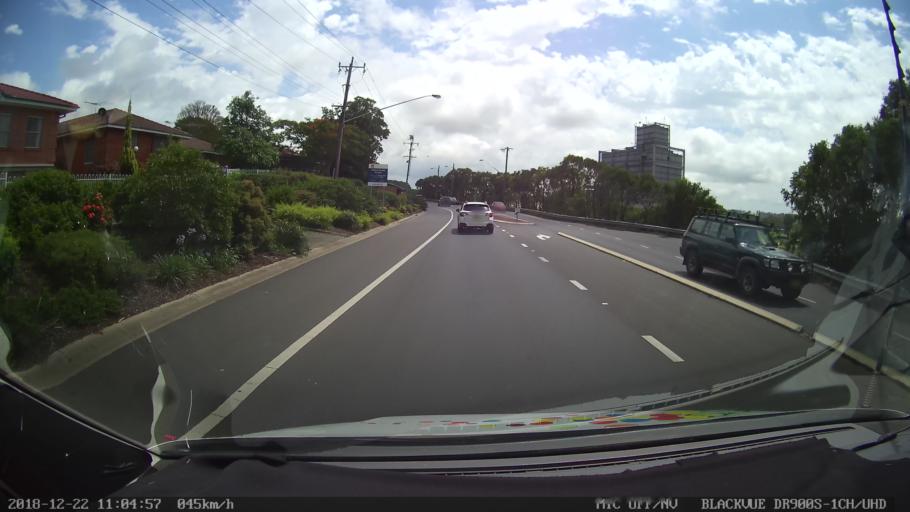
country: AU
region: New South Wales
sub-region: Clarence Valley
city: Grafton
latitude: -29.7014
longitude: 152.9418
